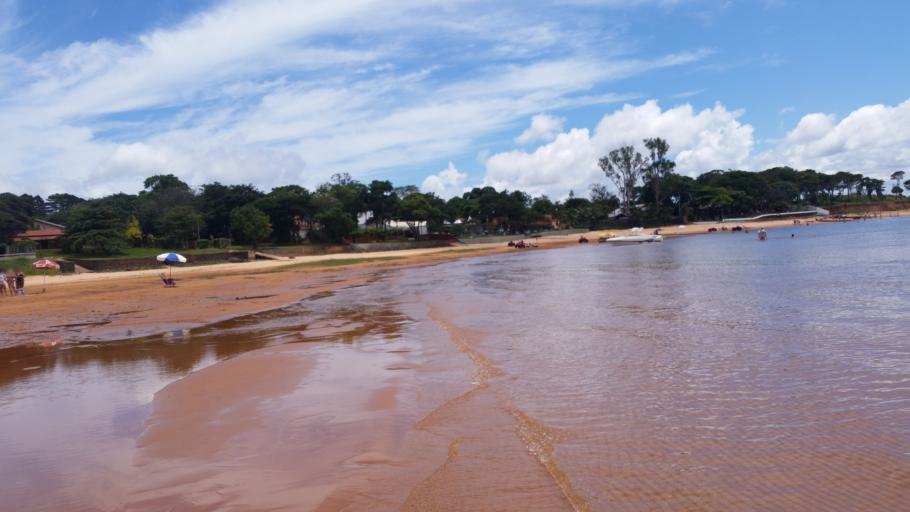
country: BR
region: Sao Paulo
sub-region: Itai
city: Itai
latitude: -23.2793
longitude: -49.0192
